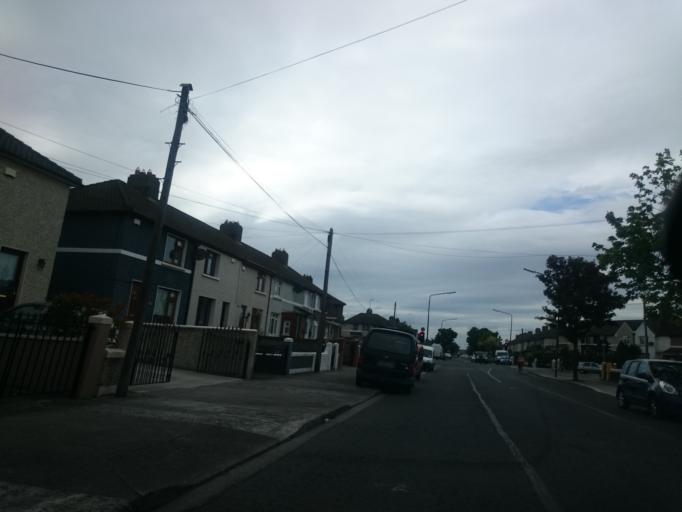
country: IE
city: Greenhills
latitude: 53.3244
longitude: -6.3016
